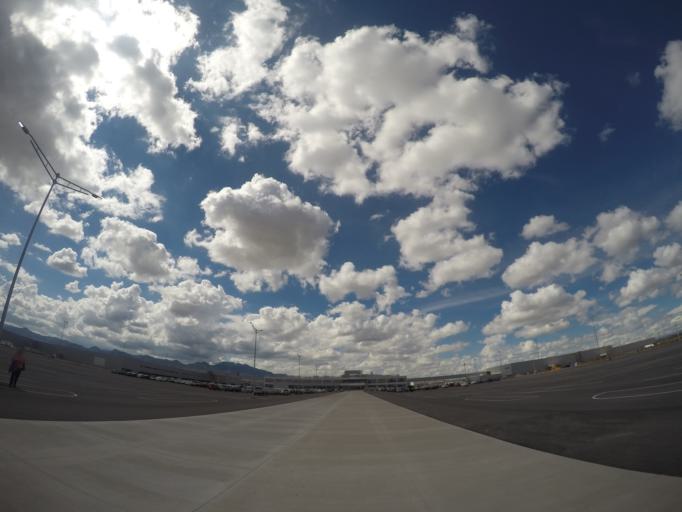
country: MX
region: San Luis Potosi
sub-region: Zaragoza
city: Cerro Gordo
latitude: 21.9664
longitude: -100.8460
